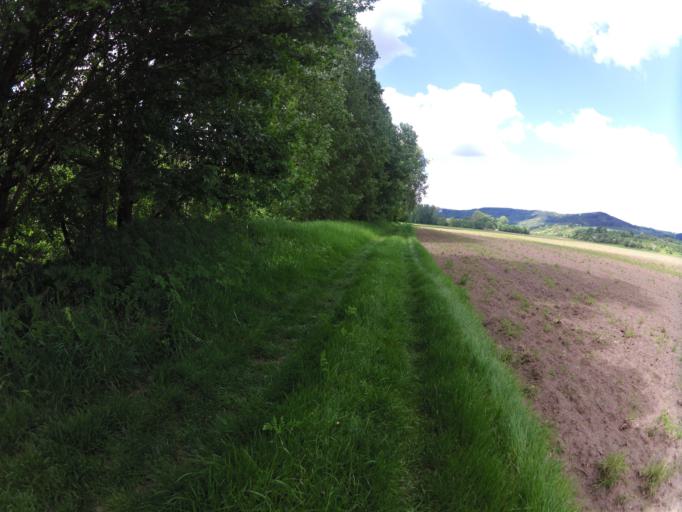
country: DE
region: Thuringia
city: Treffurt
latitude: 51.1125
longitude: 10.2516
